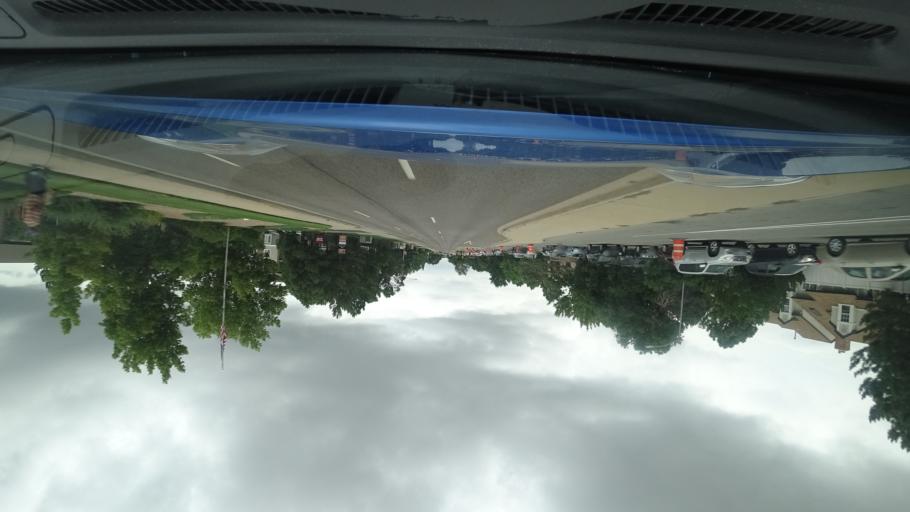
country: US
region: Colorado
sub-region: Adams County
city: Aurora
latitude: 39.6983
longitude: -104.8098
